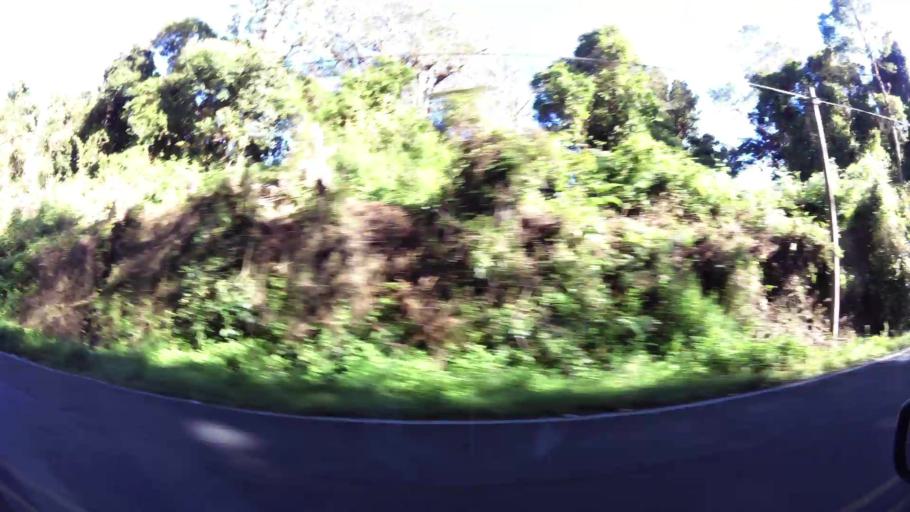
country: CR
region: San Jose
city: San Marcos
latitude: 9.7012
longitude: -83.9371
